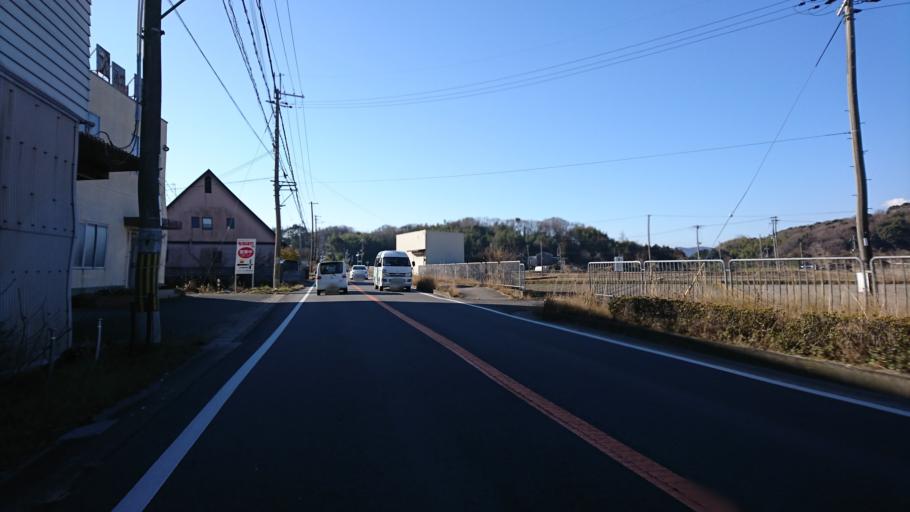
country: JP
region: Hyogo
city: Kakogawacho-honmachi
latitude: 34.8252
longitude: 134.8358
